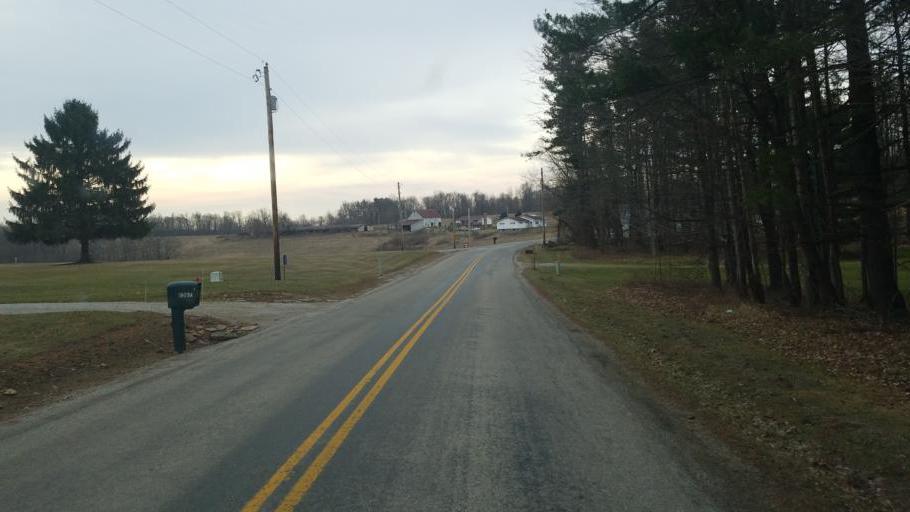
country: US
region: Ohio
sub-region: Ashland County
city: Loudonville
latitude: 40.5702
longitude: -82.2621
